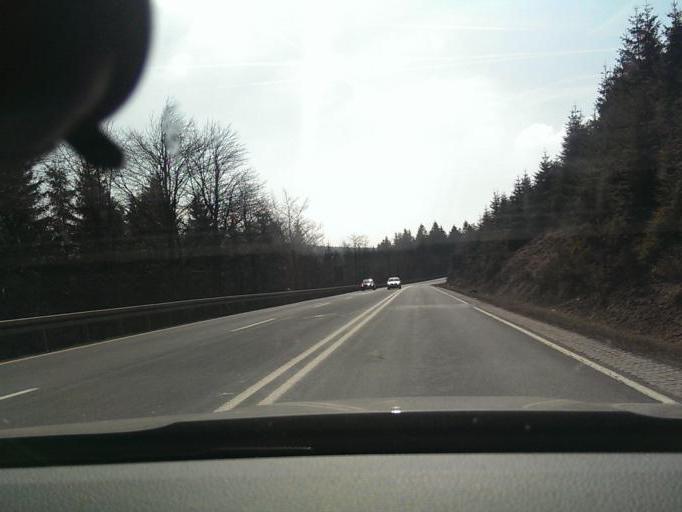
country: DE
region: Thuringia
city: Oberhof
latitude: 50.6905
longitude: 10.7117
